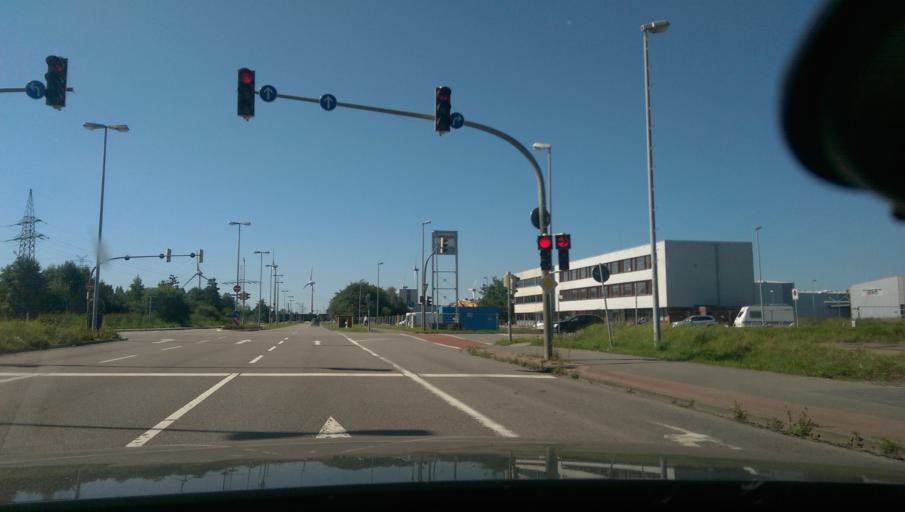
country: DE
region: Lower Saxony
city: Emden
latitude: 53.3535
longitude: 7.1707
